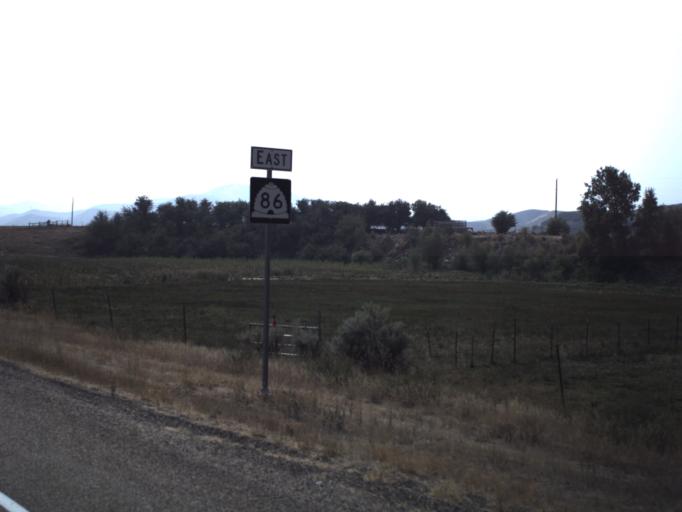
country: US
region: Utah
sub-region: Morgan County
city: Morgan
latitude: 41.0434
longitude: -111.5237
